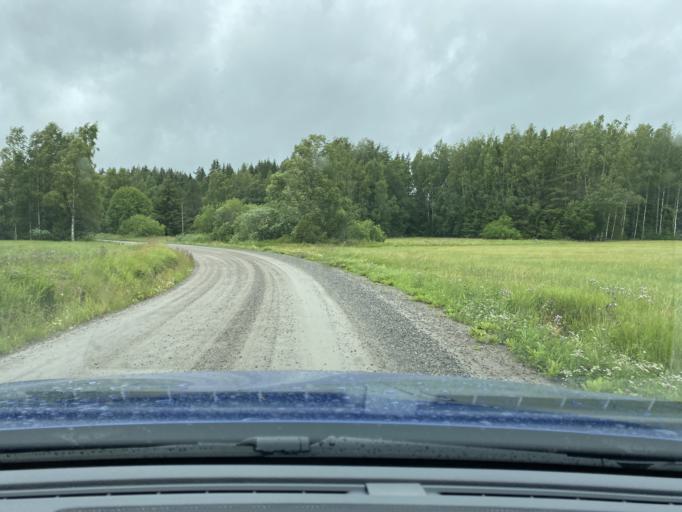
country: FI
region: Pirkanmaa
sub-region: Lounais-Pirkanmaa
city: Punkalaidun
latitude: 61.1484
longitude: 23.2164
